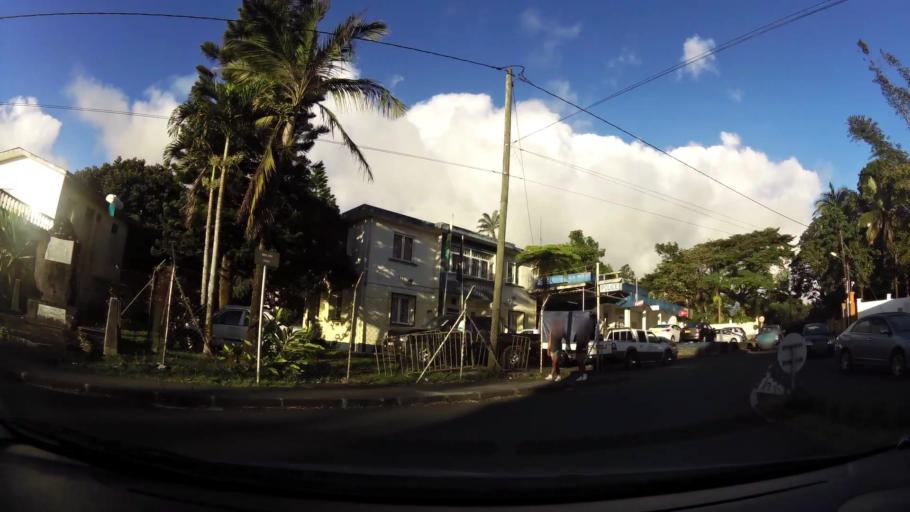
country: MU
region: Plaines Wilhems
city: Curepipe
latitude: -20.3067
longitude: 57.5257
